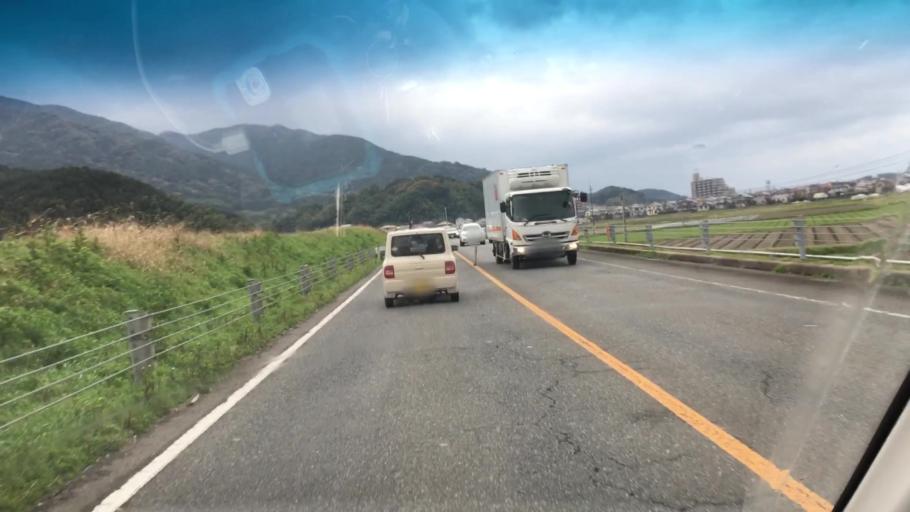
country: JP
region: Fukuoka
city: Maebaru-chuo
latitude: 33.5147
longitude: 130.1487
